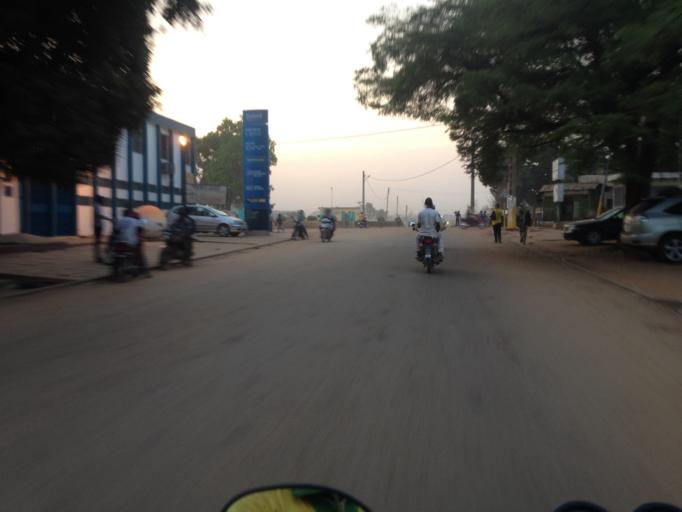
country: BJ
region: Borgou
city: Parakou
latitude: 9.3404
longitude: 2.6298
